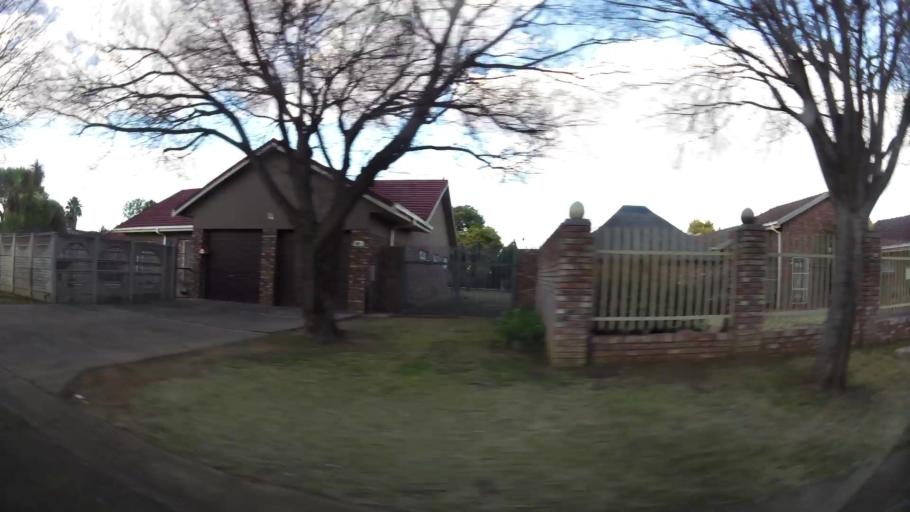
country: ZA
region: North-West
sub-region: Dr Kenneth Kaunda District Municipality
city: Potchefstroom
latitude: -26.7375
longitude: 27.0942
